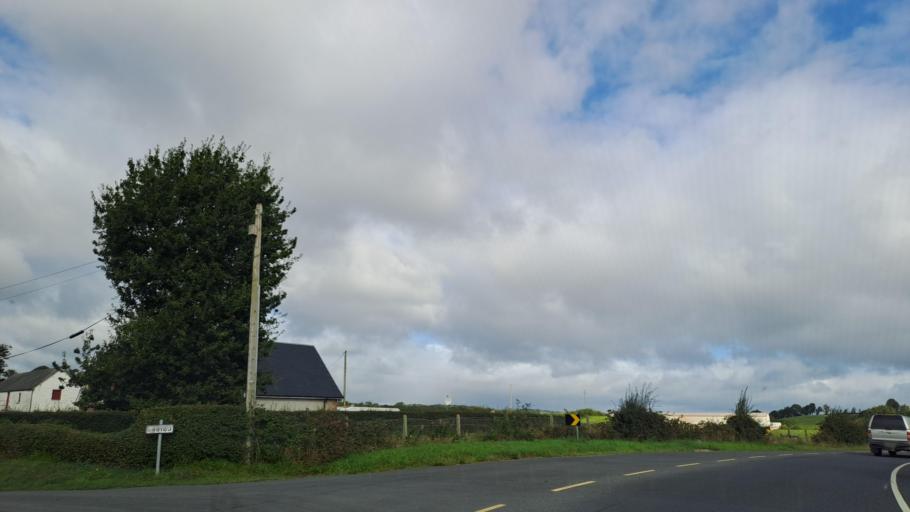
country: IE
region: Ulster
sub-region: An Cabhan
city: Kingscourt
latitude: 53.9290
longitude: -6.7803
